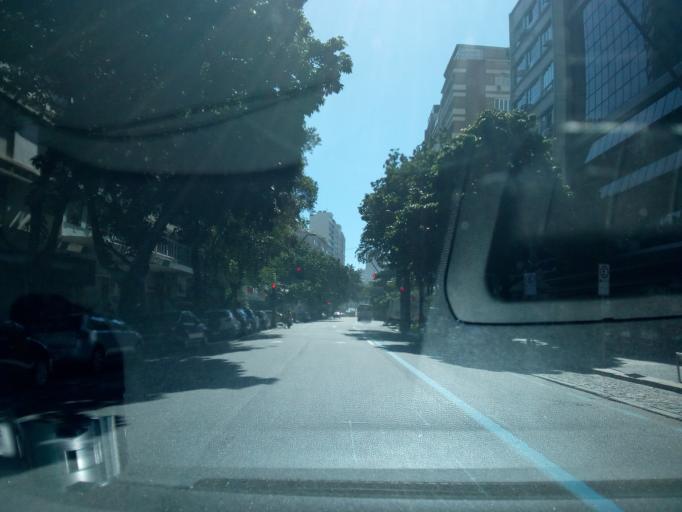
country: BR
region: Rio de Janeiro
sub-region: Rio De Janeiro
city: Rio de Janeiro
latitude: -22.9839
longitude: -43.2196
